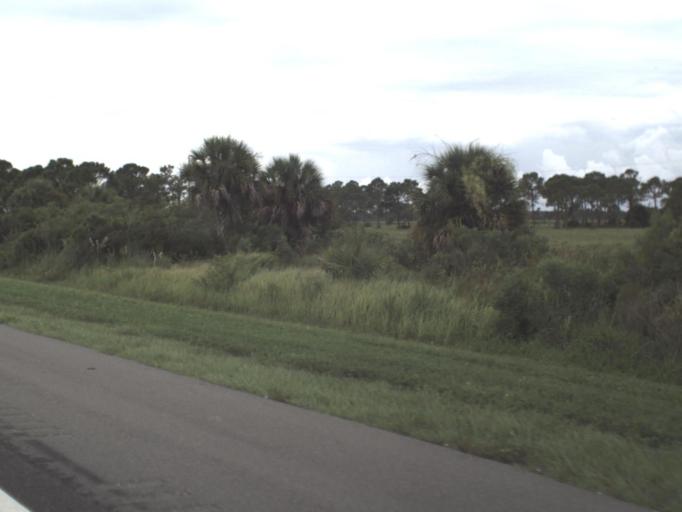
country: US
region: Florida
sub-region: Sarasota County
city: Laurel
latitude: 27.1822
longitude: -82.4369
